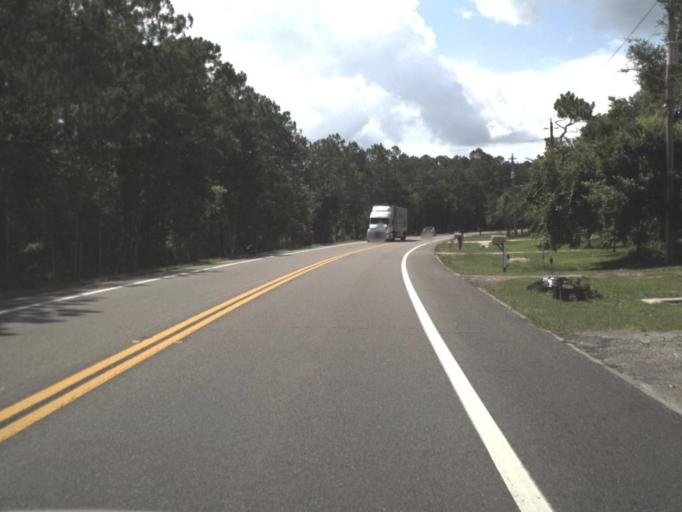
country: US
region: Florida
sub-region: Clay County
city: Green Cove Springs
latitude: 29.9740
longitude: -81.5408
